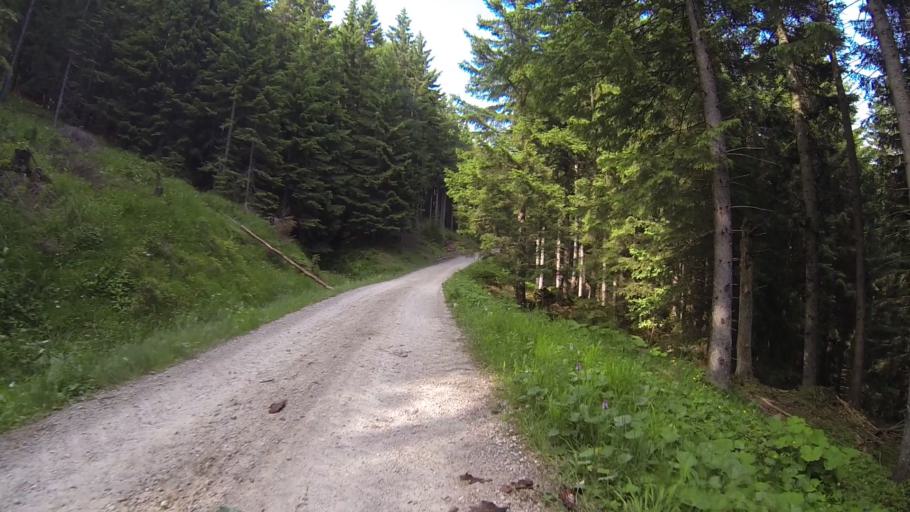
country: DE
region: Bavaria
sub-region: Swabia
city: Nesselwang
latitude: 47.5885
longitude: 10.5059
